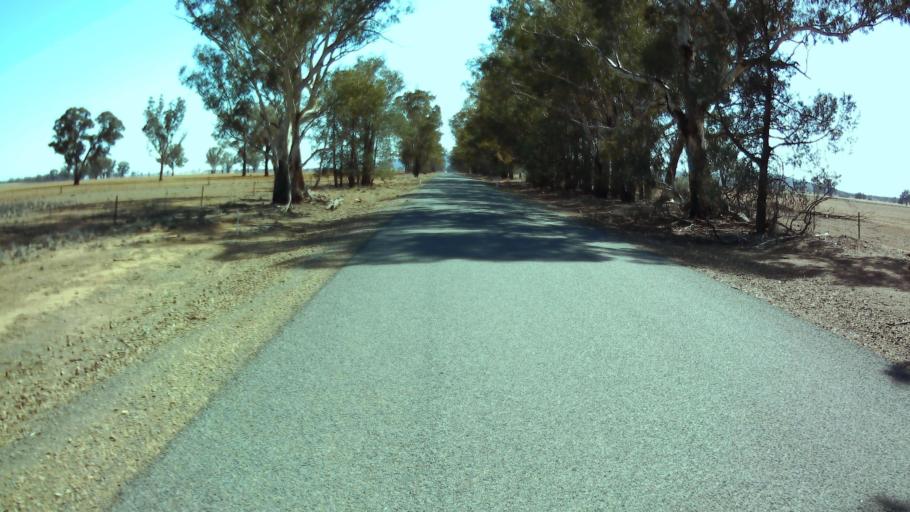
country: AU
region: New South Wales
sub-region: Weddin
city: Grenfell
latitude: -33.7209
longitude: 147.8997
